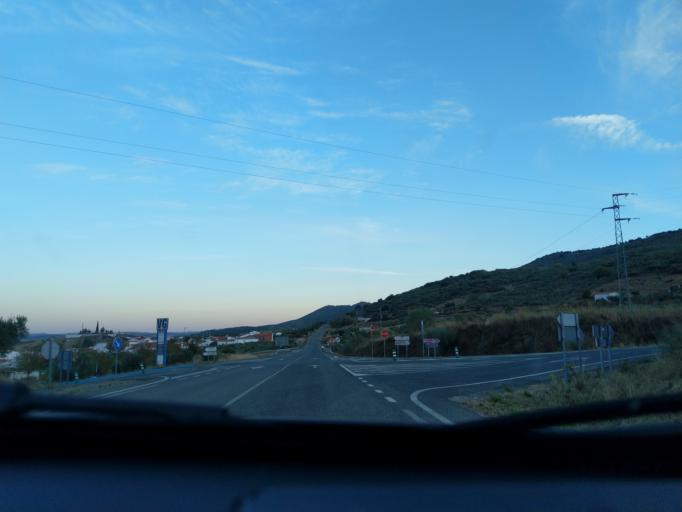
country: ES
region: Extremadura
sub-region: Provincia de Badajoz
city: Reina
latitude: 38.1533
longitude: -5.9025
